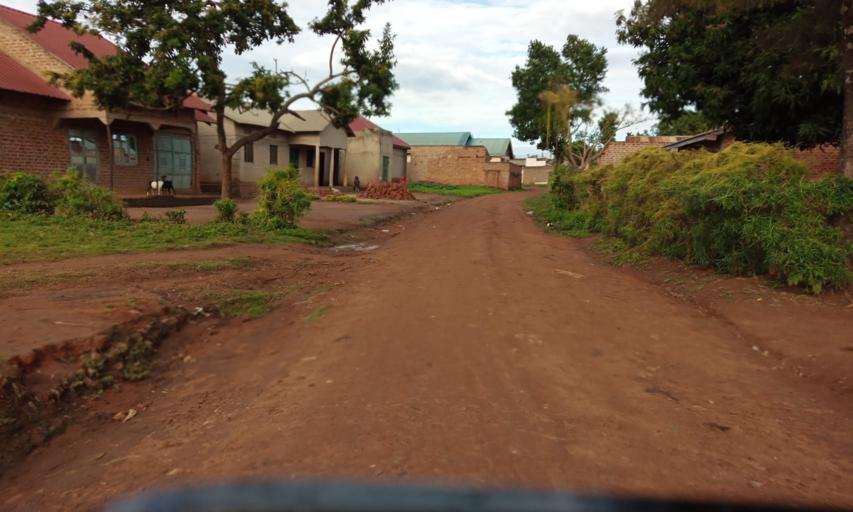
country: UG
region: Eastern Region
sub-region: Mbale District
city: Mbale
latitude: 1.1459
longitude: 34.1660
